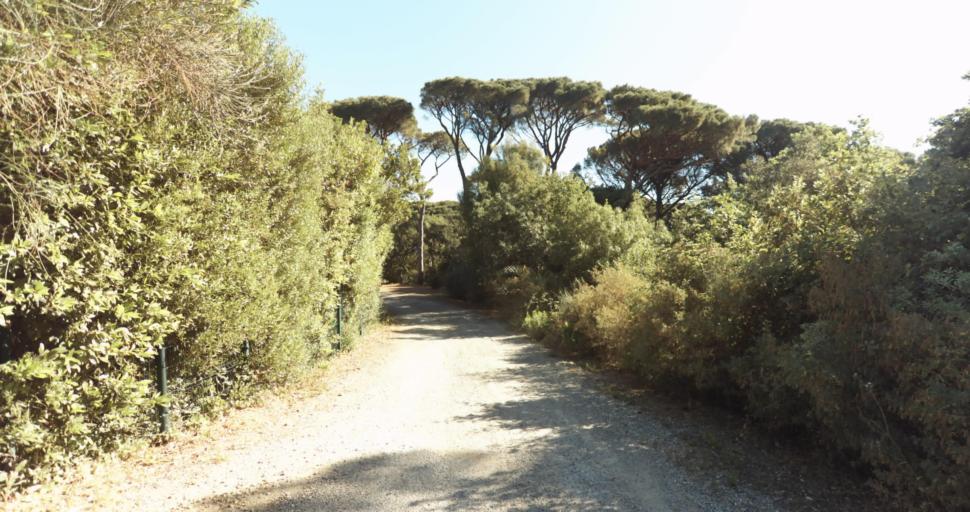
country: FR
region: Provence-Alpes-Cote d'Azur
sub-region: Departement du Var
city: Saint-Tropez
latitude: 43.2579
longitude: 6.6210
